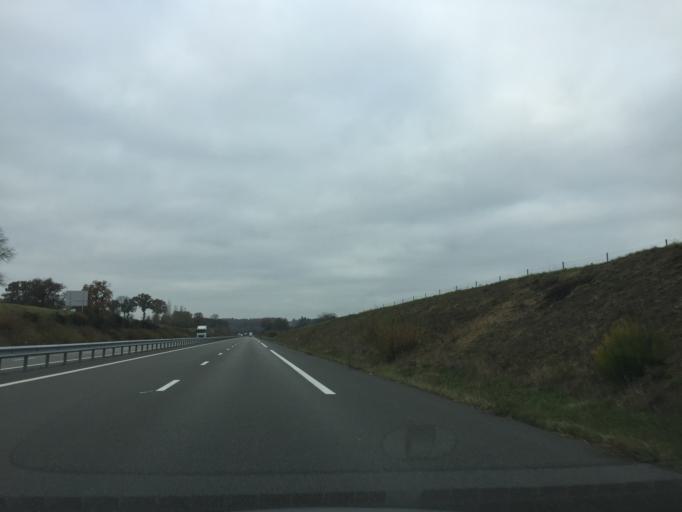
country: FR
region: Limousin
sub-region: Departement de la Creuse
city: Chambon-sur-Voueize
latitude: 46.2450
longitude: 2.3432
